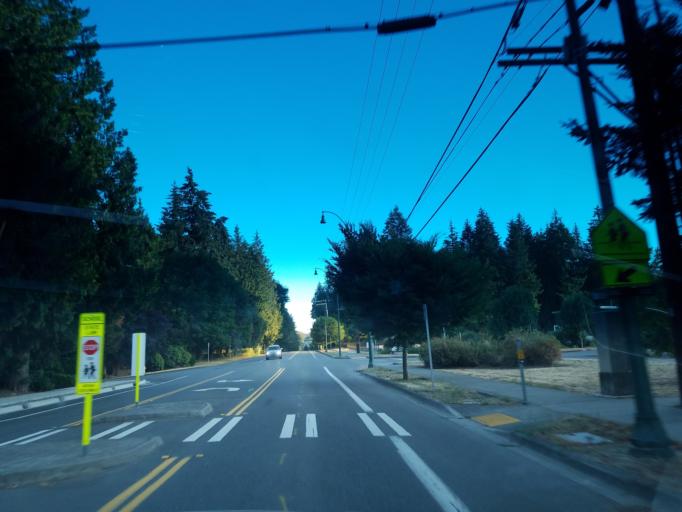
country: US
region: Washington
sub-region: King County
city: City of Sammamish
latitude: 47.6200
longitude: -122.0139
